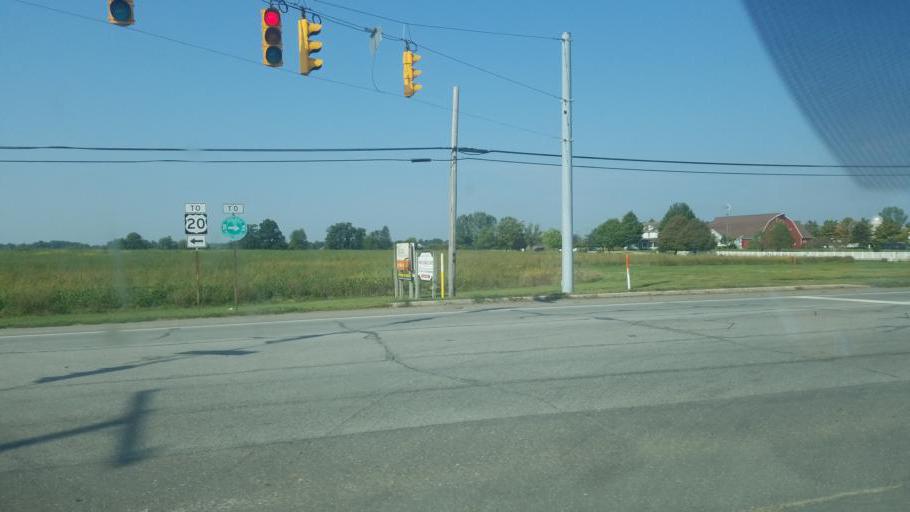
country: US
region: Indiana
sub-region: Elkhart County
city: Middlebury
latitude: 41.6691
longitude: -85.5803
